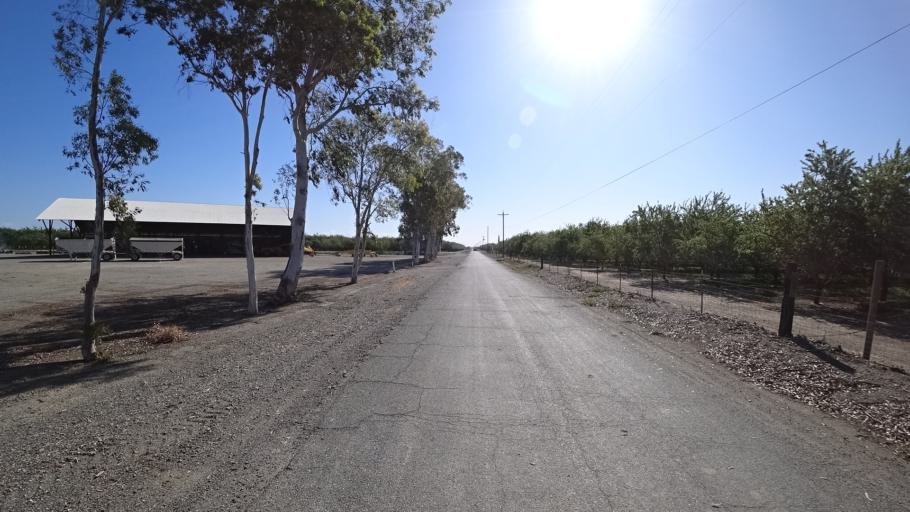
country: US
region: California
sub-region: Glenn County
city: Hamilton City
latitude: 39.6782
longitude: -122.0719
